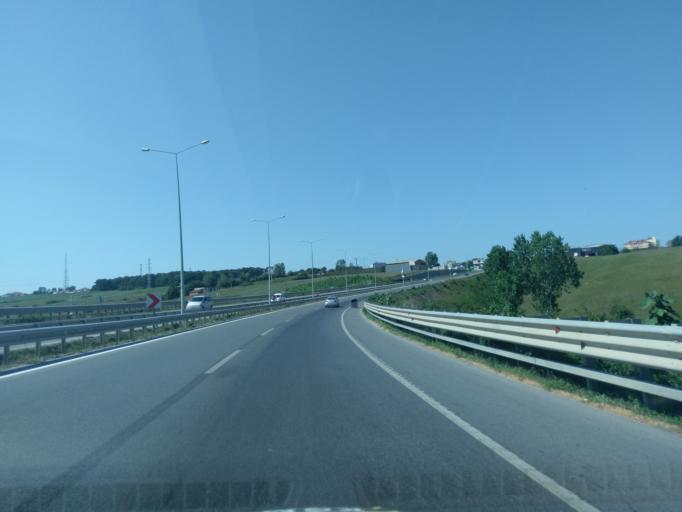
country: TR
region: Samsun
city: Bafra
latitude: 41.5417
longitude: 35.9323
